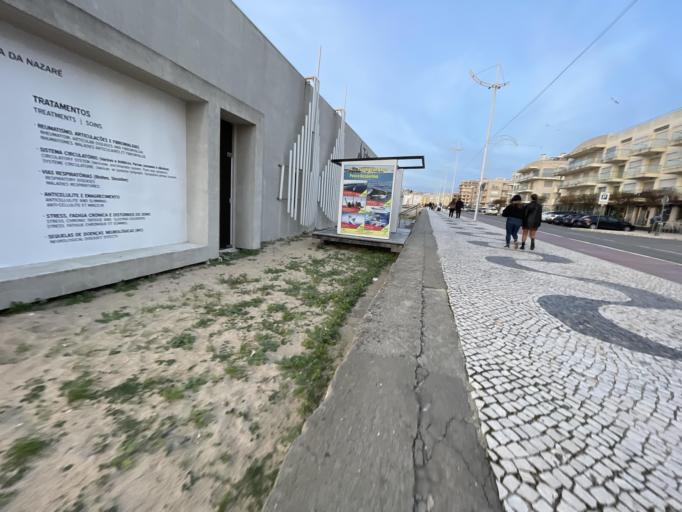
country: PT
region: Leiria
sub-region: Nazare
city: Nazare
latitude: 39.5906
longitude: -9.0739
